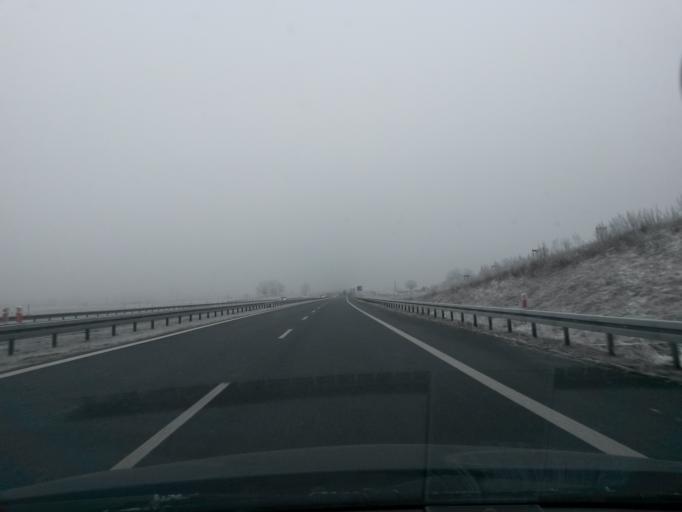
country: PL
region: Greater Poland Voivodeship
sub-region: Powiat gnieznienski
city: Lubowo
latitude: 52.4924
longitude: 17.4420
